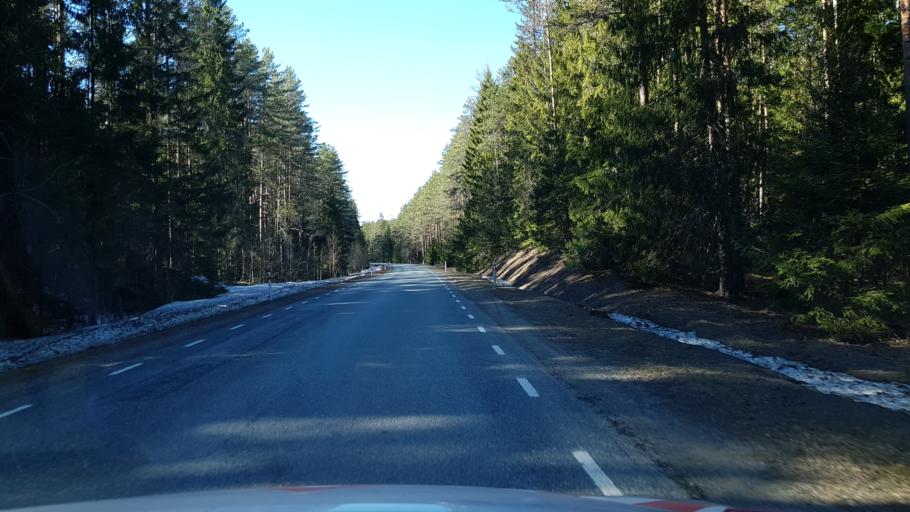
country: EE
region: Laeaene-Virumaa
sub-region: Vinni vald
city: Vinni
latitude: 59.2597
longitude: 26.6831
